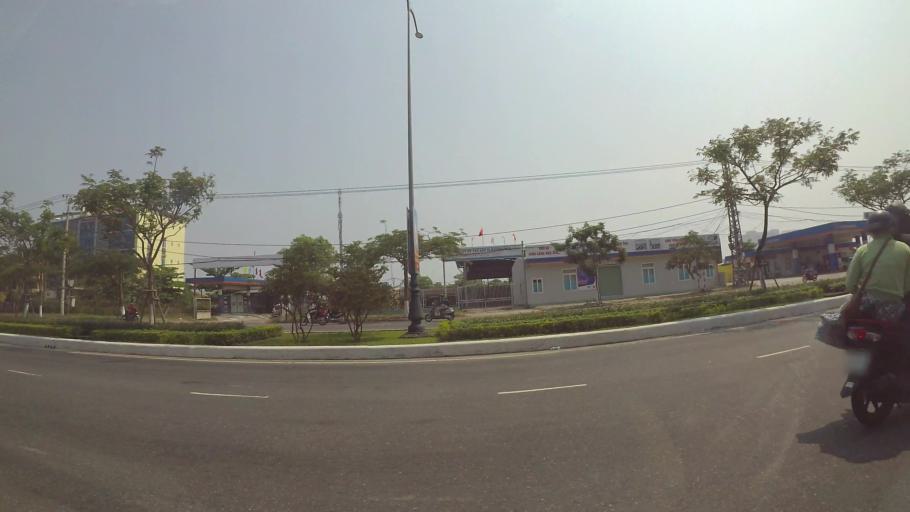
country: VN
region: Da Nang
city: Ngu Hanh Son
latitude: 16.0270
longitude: 108.2486
